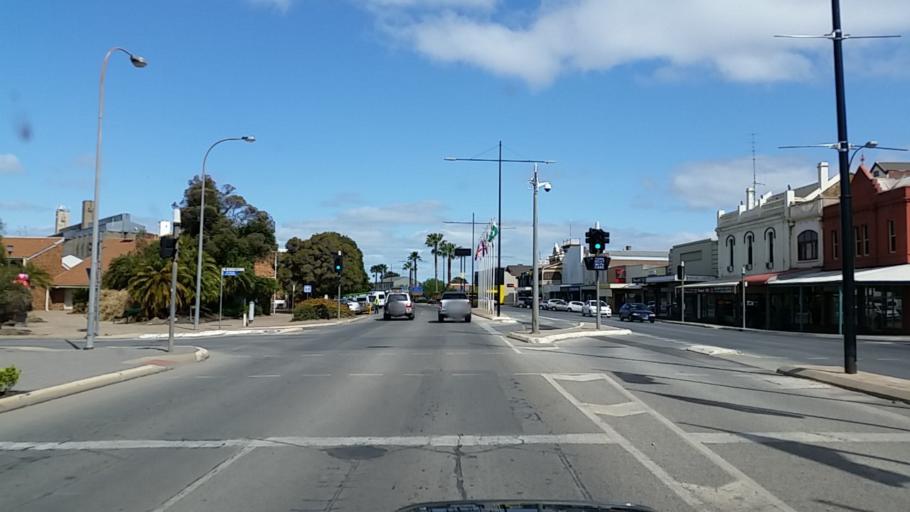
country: AU
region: South Australia
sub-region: Port Pirie City and Dists
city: Port Pirie
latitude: -33.1767
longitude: 138.0102
